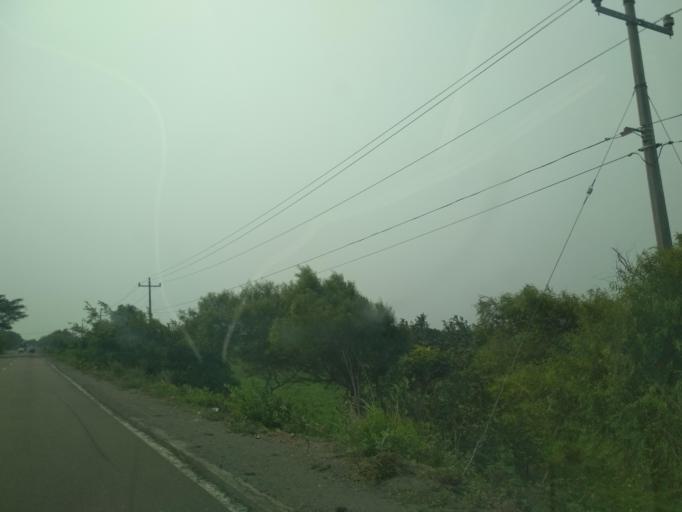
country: MX
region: Veracruz
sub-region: Veracruz
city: Delfino Victoria (Santa Fe)
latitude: 19.2006
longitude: -96.3059
